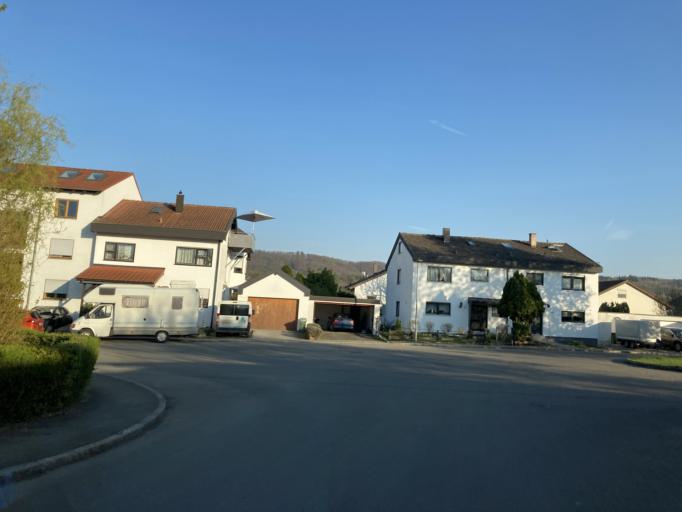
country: DE
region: Baden-Wuerttemberg
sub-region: Tuebingen Region
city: Nehren
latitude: 48.4333
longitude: 9.0724
